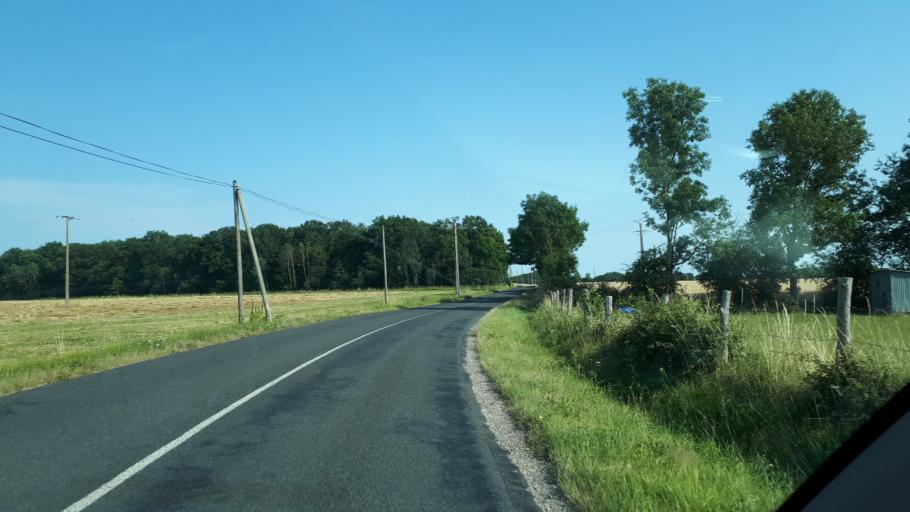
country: FR
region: Centre
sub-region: Departement du Loir-et-Cher
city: Droue
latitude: 47.9830
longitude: 1.0419
